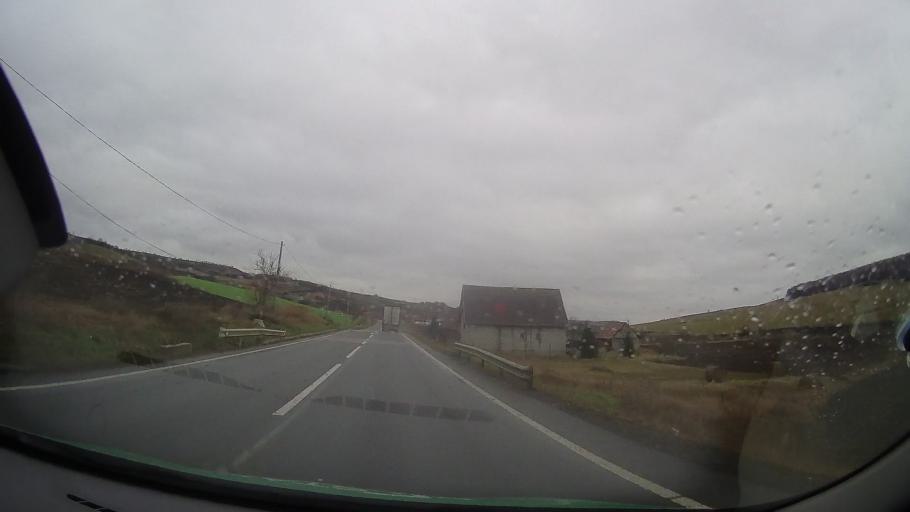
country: RO
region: Mures
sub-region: Comuna Lunca
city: Lunca
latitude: 46.8580
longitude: 24.5621
